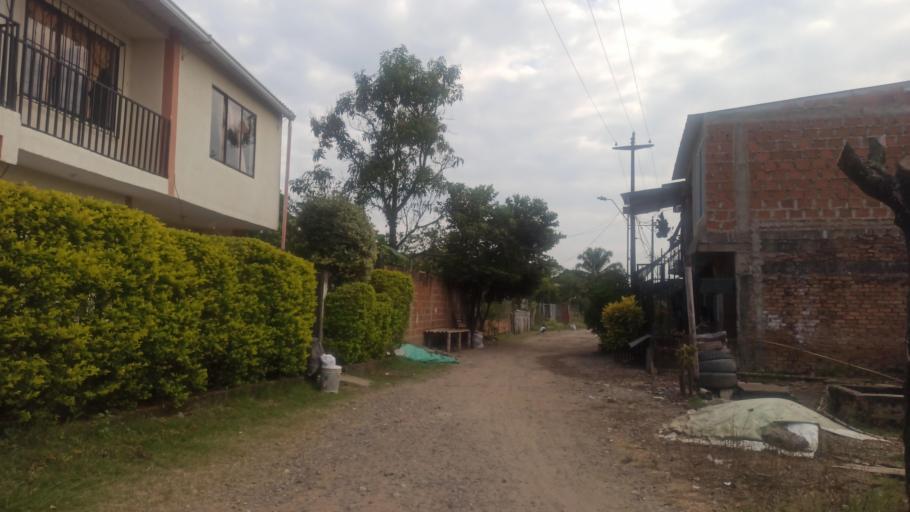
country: CO
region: Valle del Cauca
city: Jamundi
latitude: 3.1292
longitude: -76.5594
